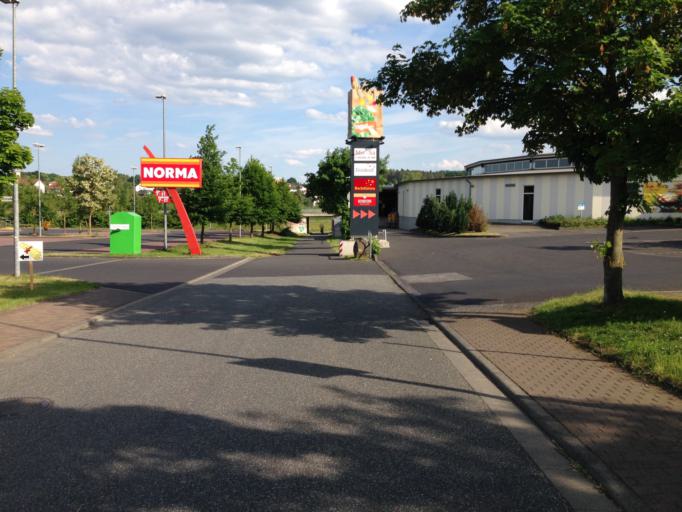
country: DE
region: Hesse
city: Staufenberg
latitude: 50.6576
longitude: 8.7353
